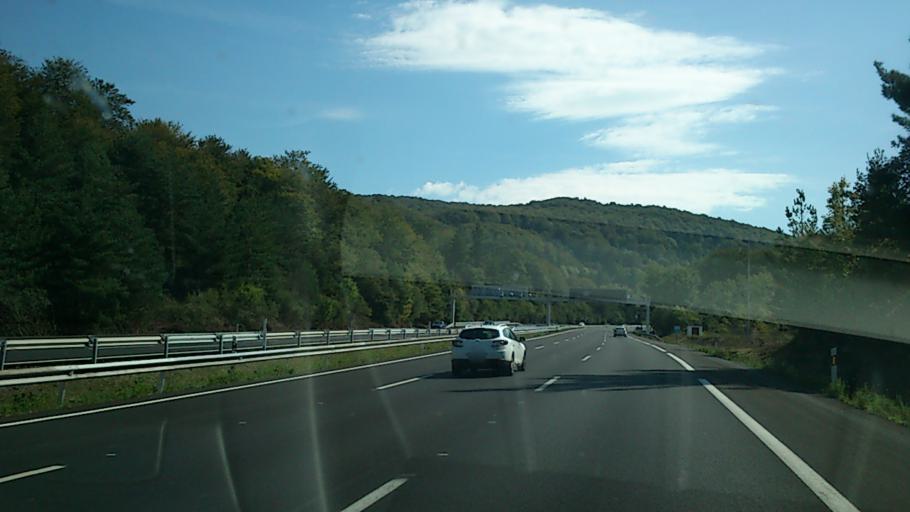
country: ES
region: Basque Country
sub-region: Provincia de Alava
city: Murguia
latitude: 42.9912
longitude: -2.8745
